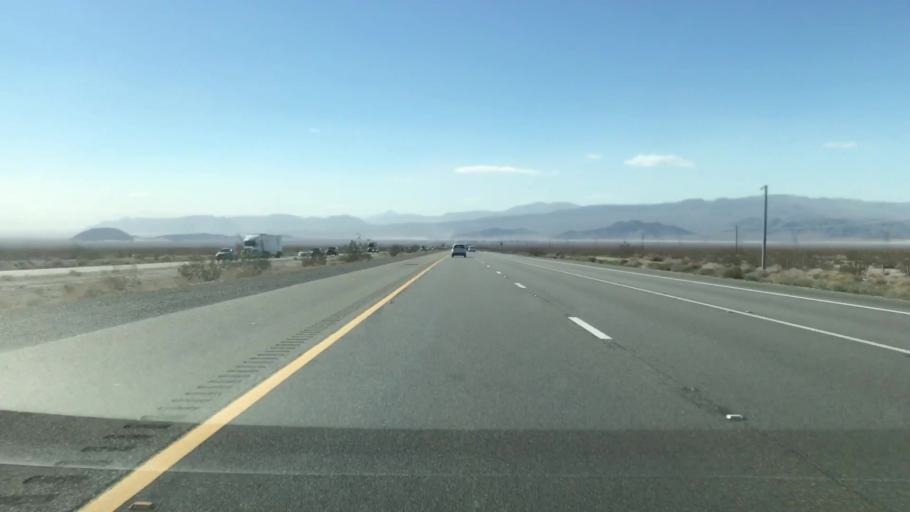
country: US
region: Nevada
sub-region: Clark County
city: Sandy Valley
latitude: 35.3266
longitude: -115.9785
